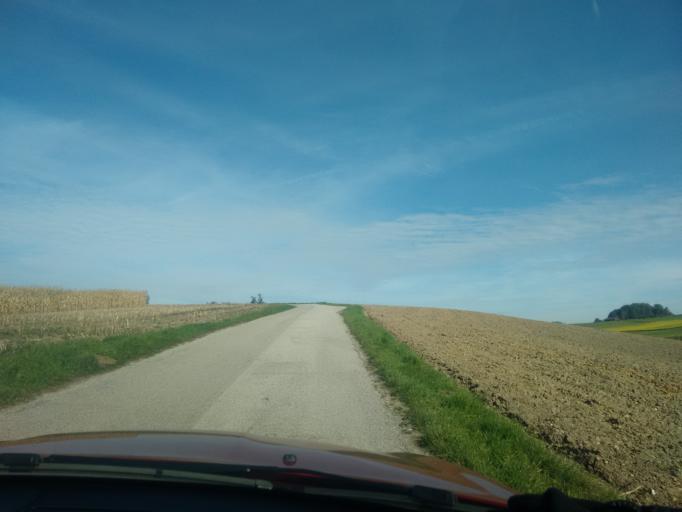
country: AT
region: Upper Austria
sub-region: Politischer Bezirk Vocklabruck
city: Manning
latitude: 48.0755
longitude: 13.6399
